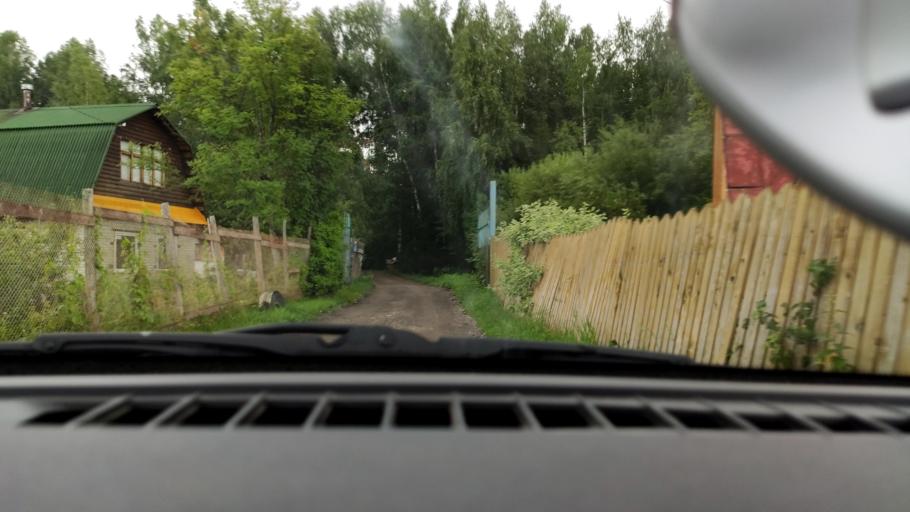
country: RU
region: Perm
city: Overyata
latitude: 58.0530
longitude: 55.9767
